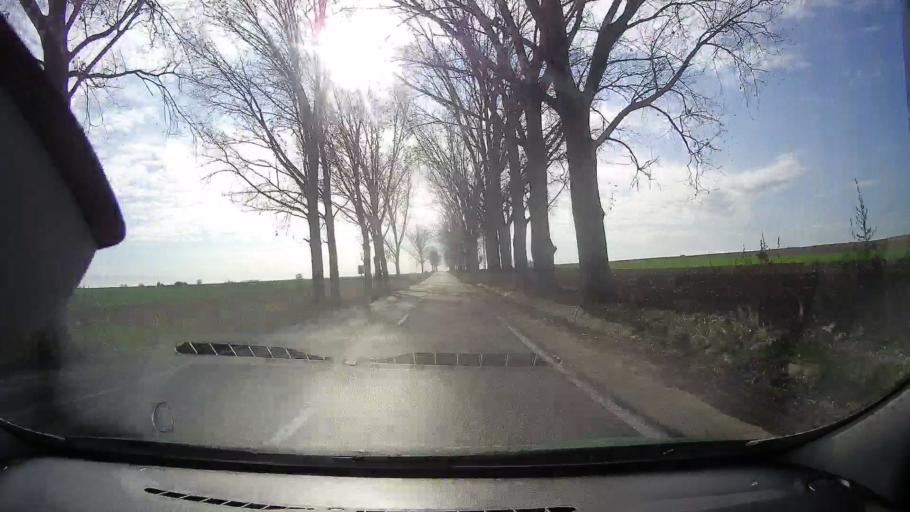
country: RO
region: Tulcea
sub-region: Comuna Valea Nucarilor
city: Agighiol
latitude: 45.0013
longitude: 28.8859
